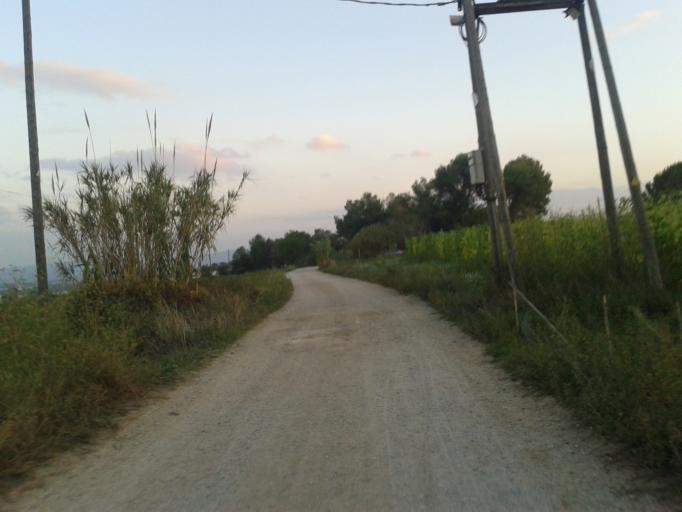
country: ES
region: Catalonia
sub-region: Provincia de Barcelona
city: Sentmenat
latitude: 41.6202
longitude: 2.1314
